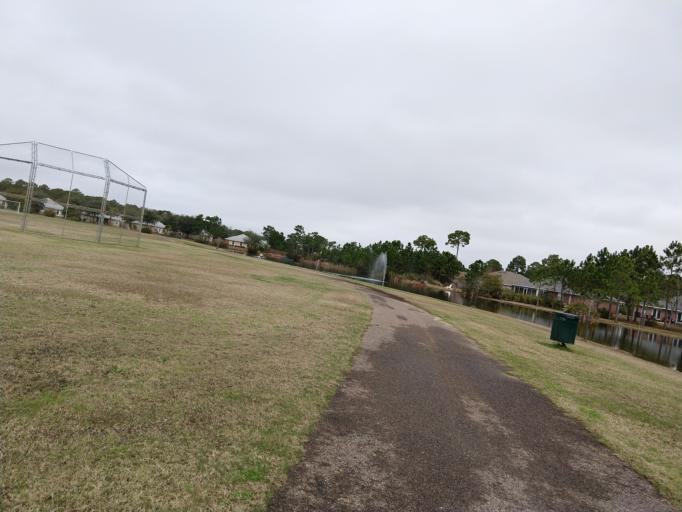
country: US
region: Florida
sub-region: Walton County
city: Miramar Beach
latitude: 30.4115
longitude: -86.3079
